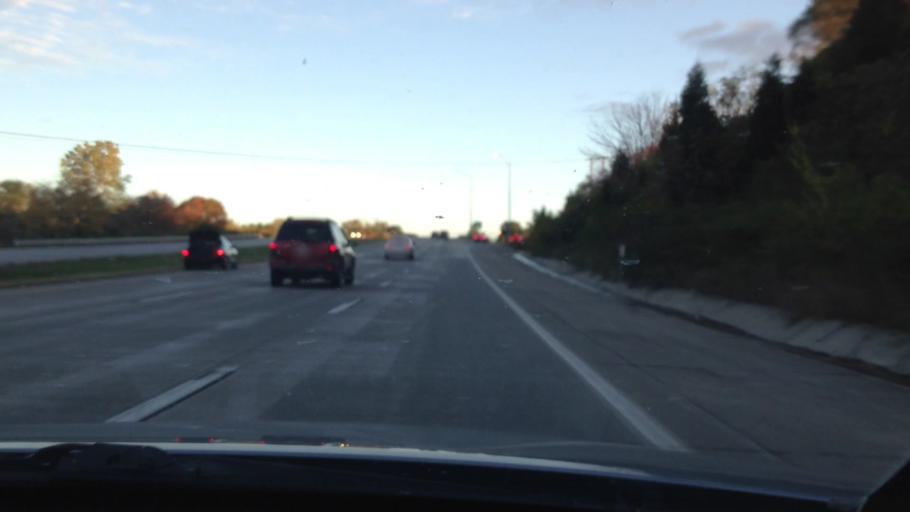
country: US
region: Missouri
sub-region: Jackson County
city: Raytown
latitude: 39.0122
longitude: -94.4921
